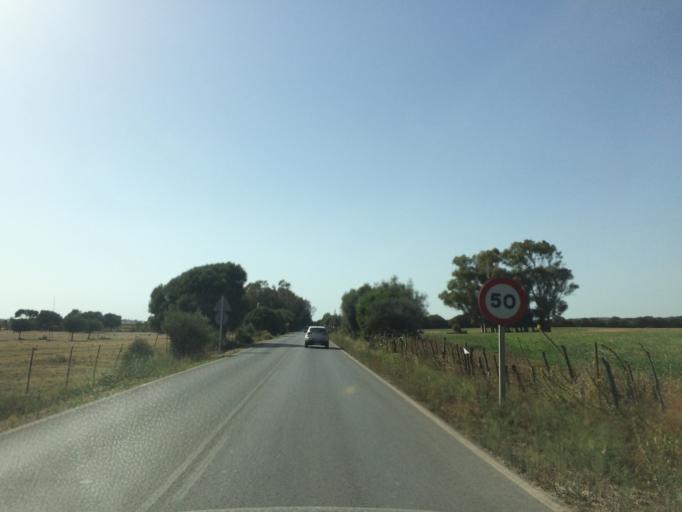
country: ES
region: Andalusia
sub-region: Provincia de Cadiz
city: Vejer de la Frontera
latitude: 36.2121
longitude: -6.0332
